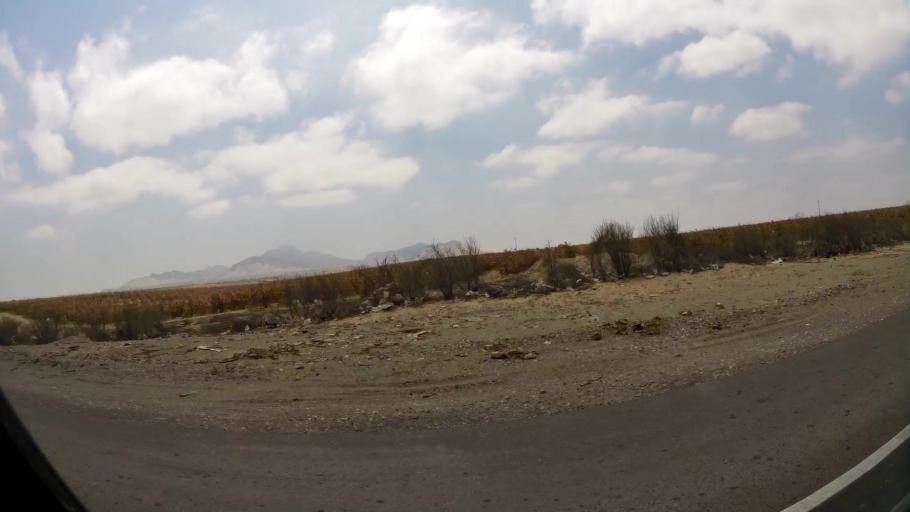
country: PE
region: La Libertad
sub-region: Ascope
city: Paijan
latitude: -7.6572
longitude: -79.3393
